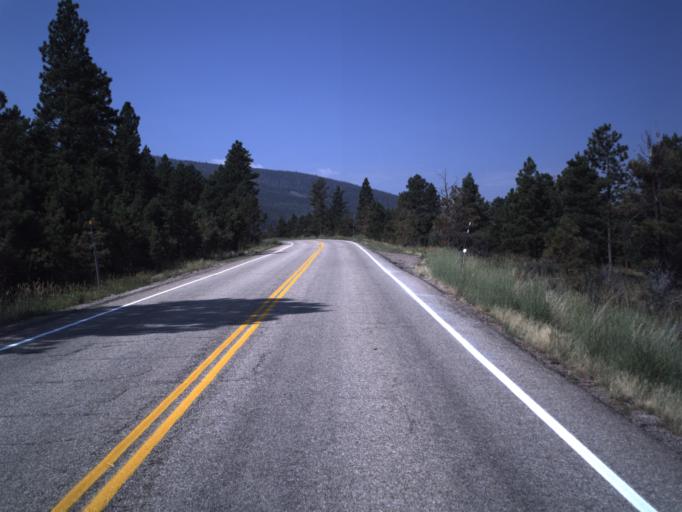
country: US
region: Utah
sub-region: Daggett County
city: Manila
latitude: 40.8727
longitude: -109.4682
